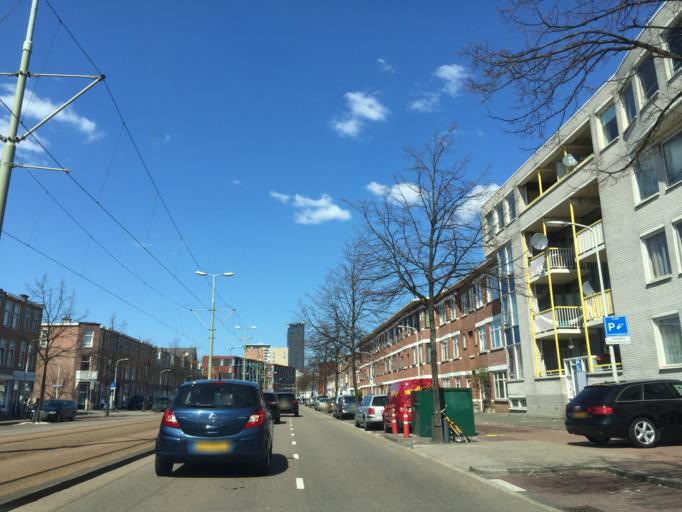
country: NL
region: South Holland
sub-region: Gemeente Rijswijk
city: Rijswijk
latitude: 52.0633
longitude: 4.3317
